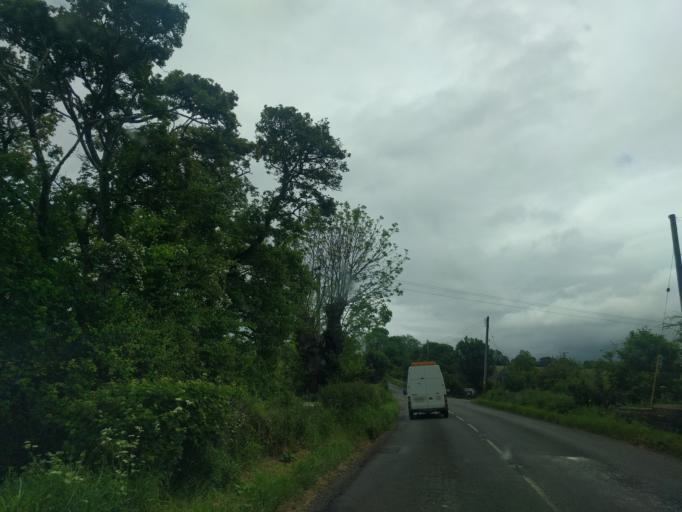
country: GB
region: England
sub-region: Somerset
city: Langport
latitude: 51.0444
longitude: -2.7995
